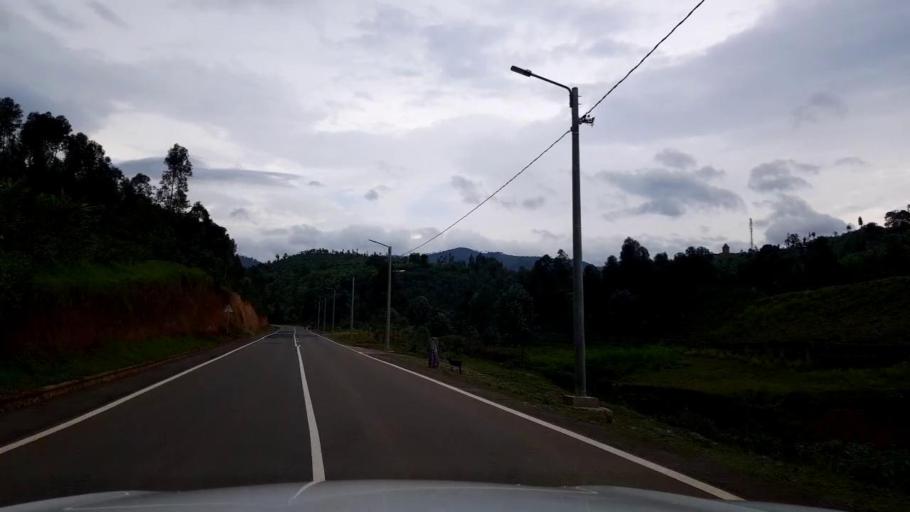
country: RW
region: Western Province
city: Kibuye
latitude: -2.0198
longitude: 29.3908
